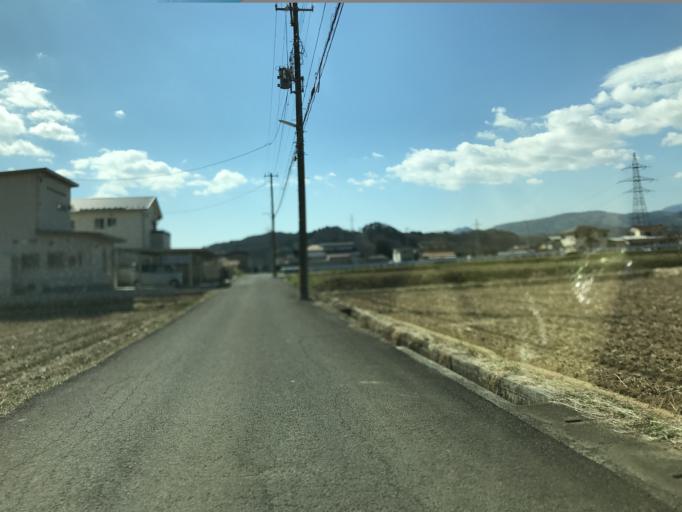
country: JP
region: Fukushima
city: Fukushima-shi
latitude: 37.7360
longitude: 140.4137
